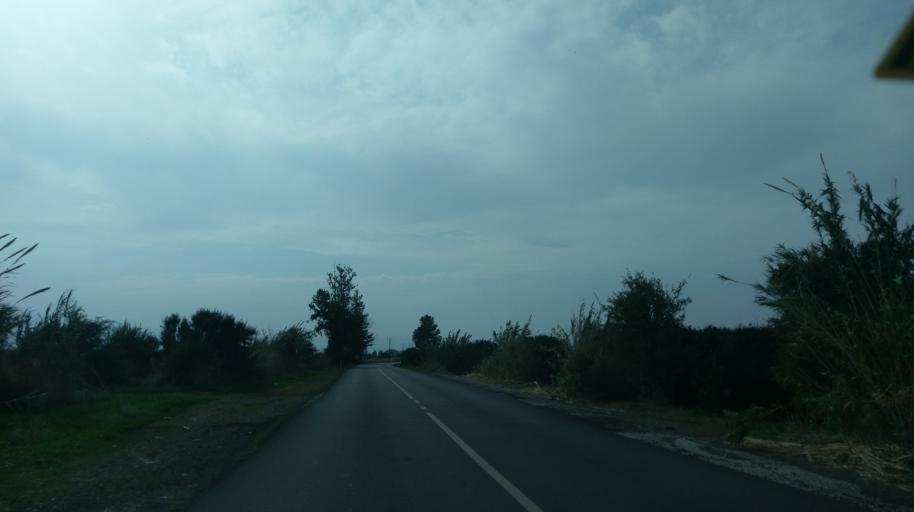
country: CY
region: Lefkosia
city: Astromeritis
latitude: 35.1753
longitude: 33.0230
